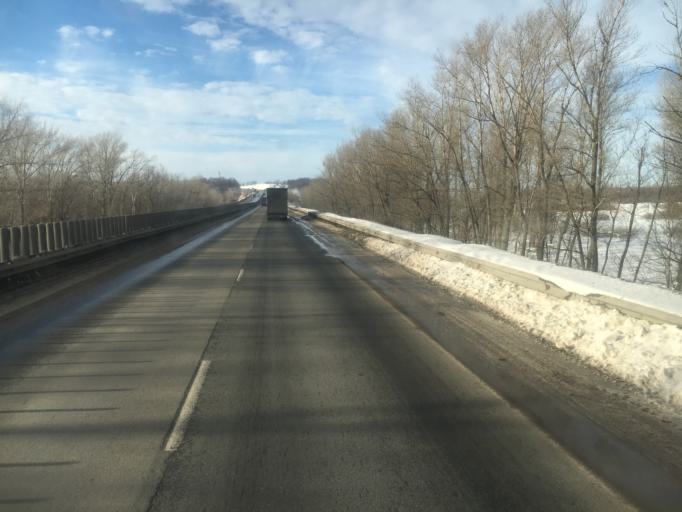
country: RU
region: Samara
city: Mirnyy
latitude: 53.4411
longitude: 50.2755
